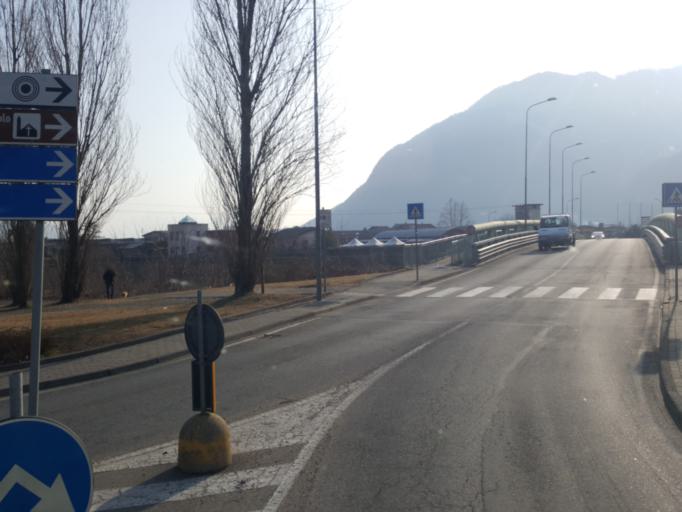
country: IT
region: Piedmont
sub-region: Provincia Verbano-Cusio-Ossola
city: Gravellona Toce
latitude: 45.9303
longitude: 8.4388
